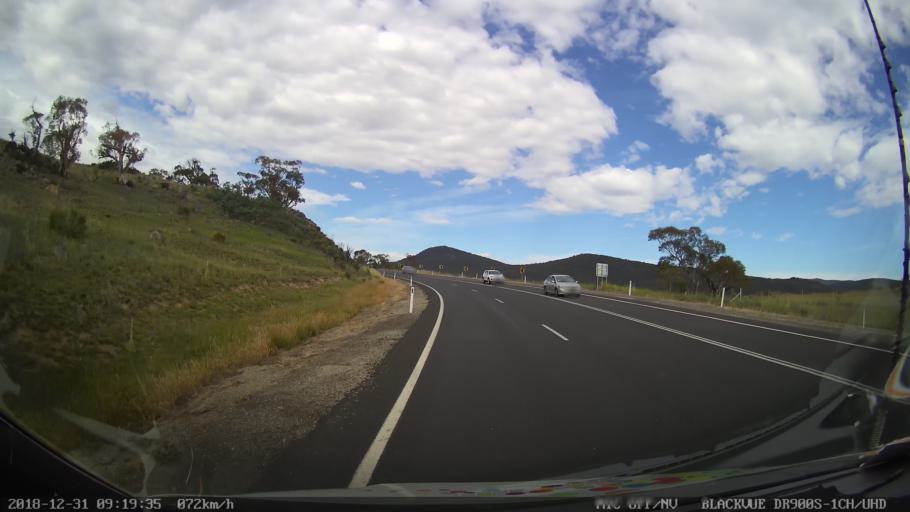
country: AU
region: New South Wales
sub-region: Snowy River
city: Jindabyne
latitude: -36.4161
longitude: 148.5843
